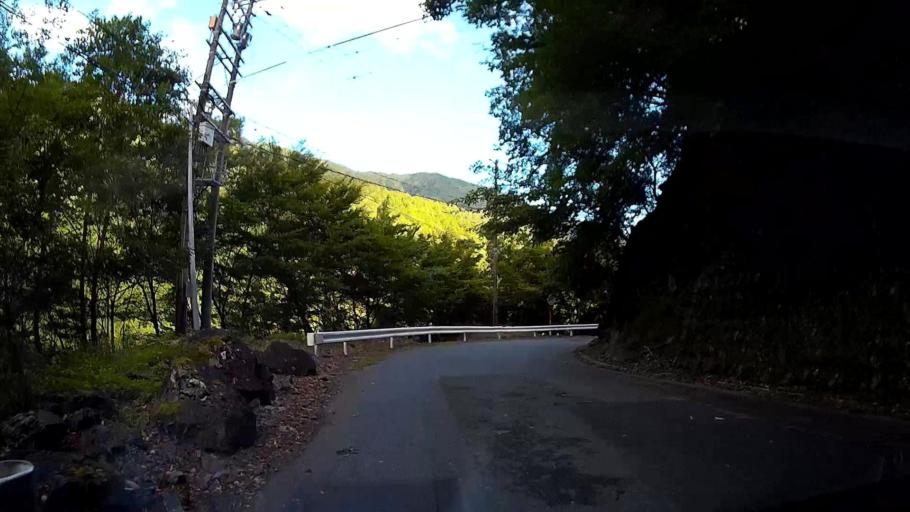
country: JP
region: Shizuoka
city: Shizuoka-shi
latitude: 35.3016
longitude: 138.2166
